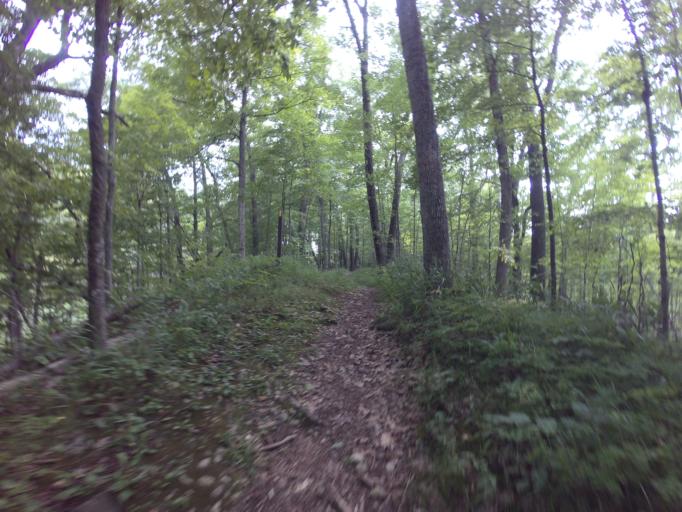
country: US
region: Wisconsin
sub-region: Washington County
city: Kewaskum
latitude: 43.5887
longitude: -88.1782
